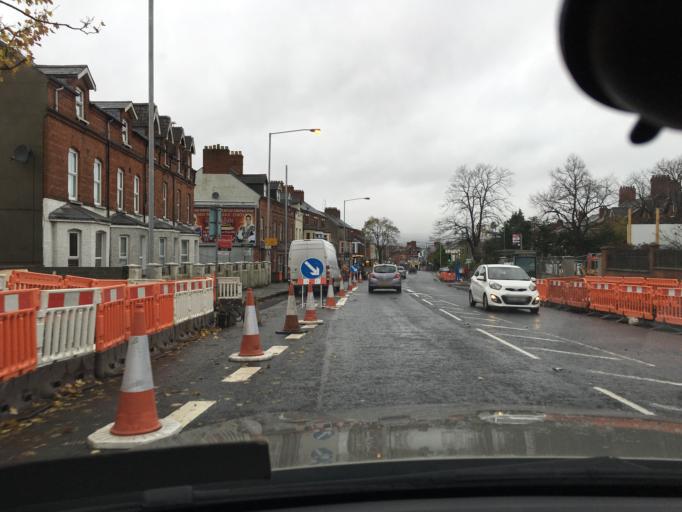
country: GB
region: Northern Ireland
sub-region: Castlereagh District
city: Castlereagh
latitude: 54.5964
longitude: -5.8824
